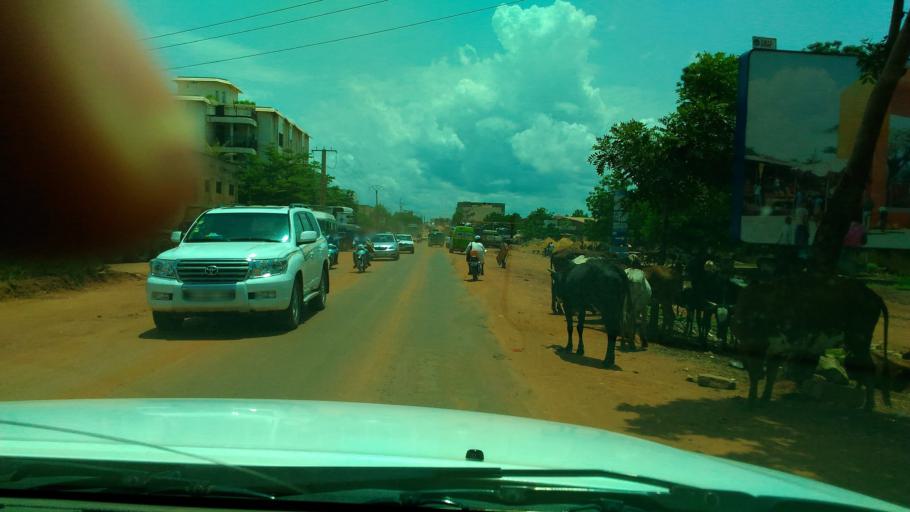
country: ML
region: Bamako
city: Bamako
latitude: 12.6698
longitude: -7.9164
